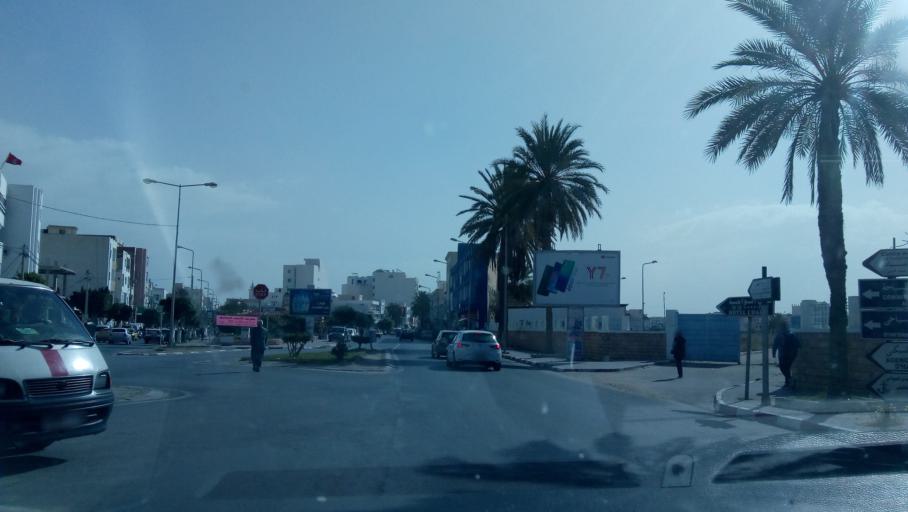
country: TN
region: Qabis
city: Gabes
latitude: 33.8850
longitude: 10.0959
